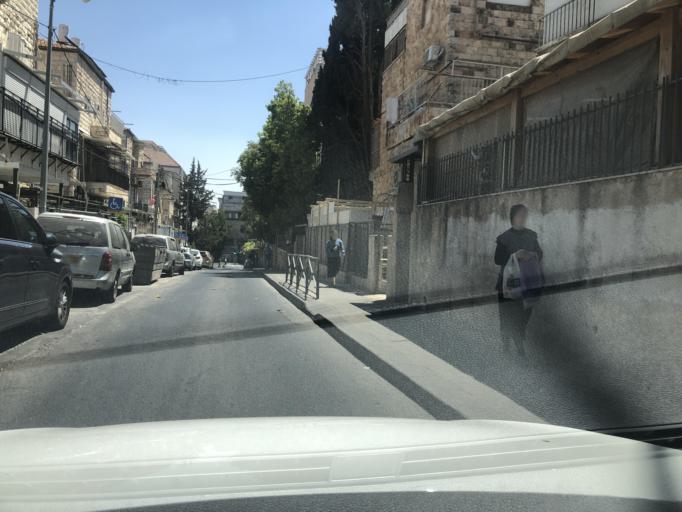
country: IL
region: Jerusalem
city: West Jerusalem
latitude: 31.7908
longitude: 35.2177
